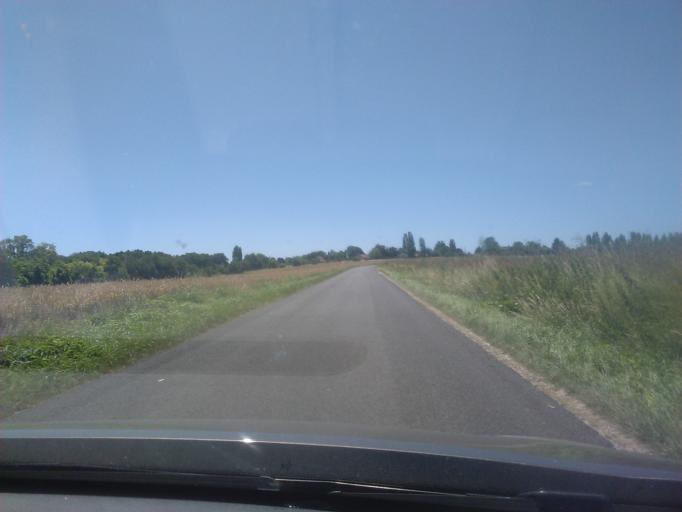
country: FR
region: Centre
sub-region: Departement du Loir-et-Cher
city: Saint-Sulpice-de-Pommeray
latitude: 47.6020
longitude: 1.2212
